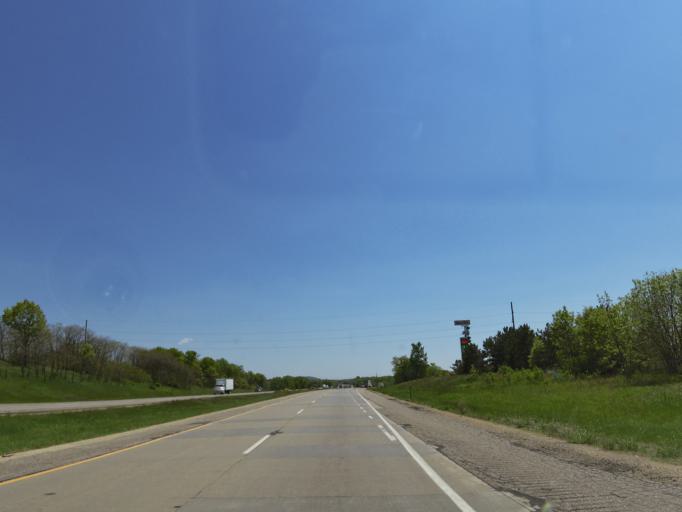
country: US
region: Wisconsin
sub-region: Juneau County
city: Mauston
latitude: 43.8009
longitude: -90.0608
